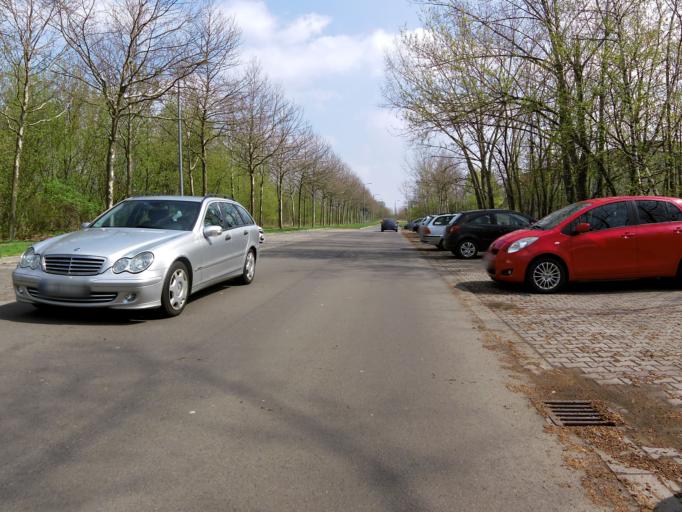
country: DE
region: Saxony
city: Markranstadt
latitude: 51.3264
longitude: 12.2683
